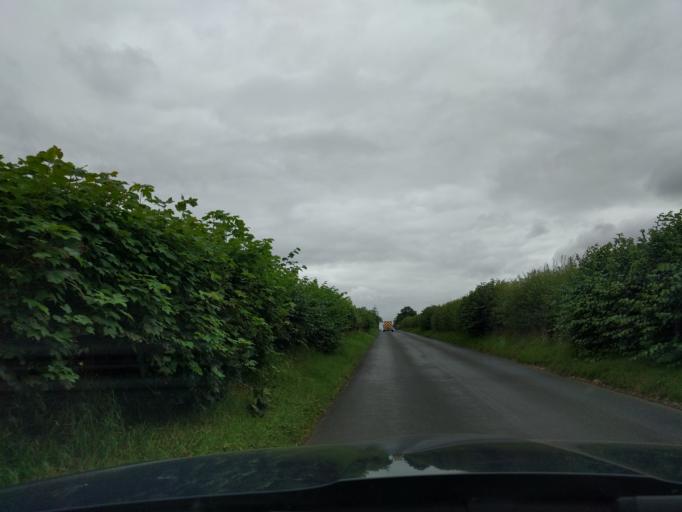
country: GB
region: England
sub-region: Northumberland
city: Berwick-Upon-Tweed
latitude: 55.7515
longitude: -2.0698
